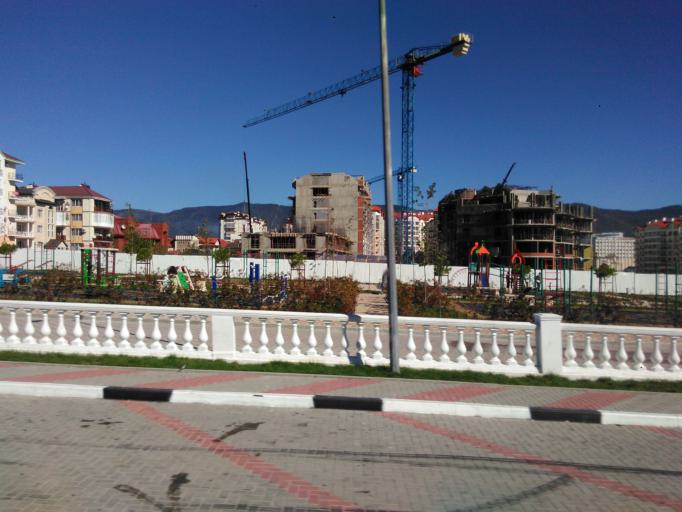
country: RU
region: Krasnodarskiy
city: Gelendzhik
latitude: 44.5485
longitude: 38.0554
